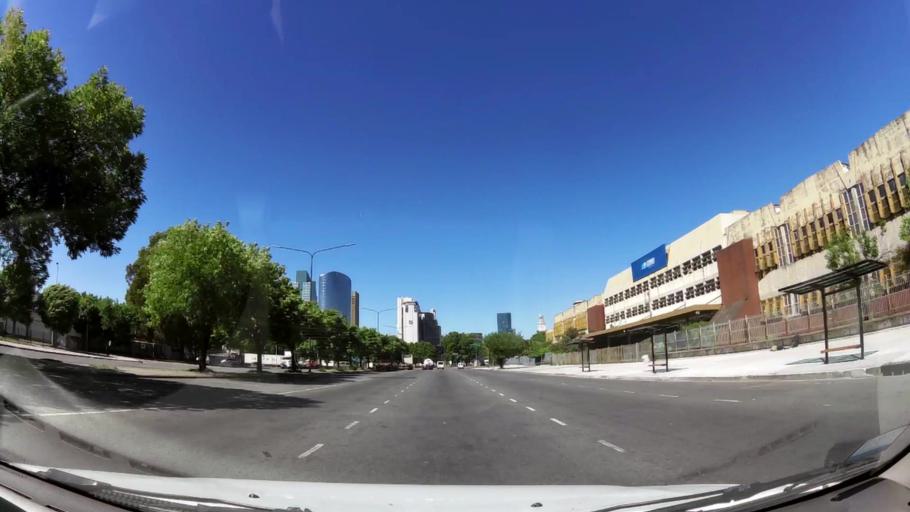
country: AR
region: Buenos Aires F.D.
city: Retiro
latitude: -34.5888
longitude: -58.3693
